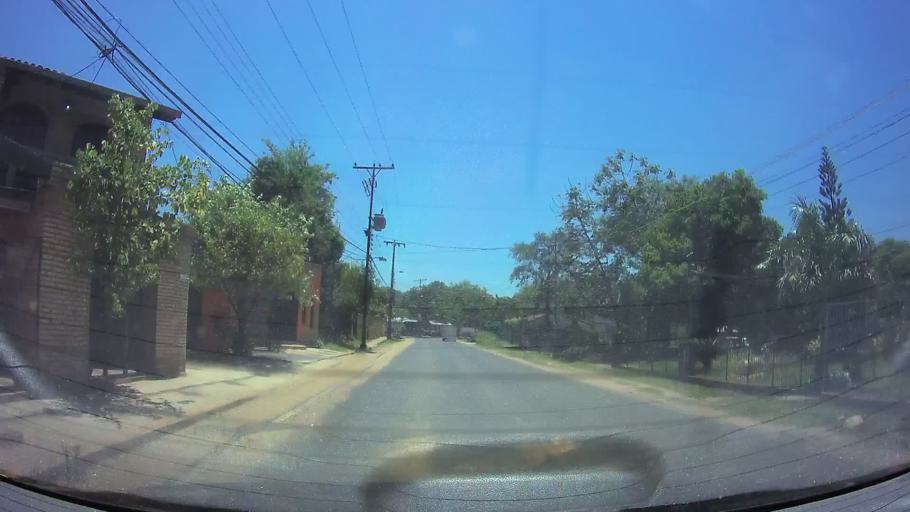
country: PY
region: Central
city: Fernando de la Mora
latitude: -25.2829
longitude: -57.5198
